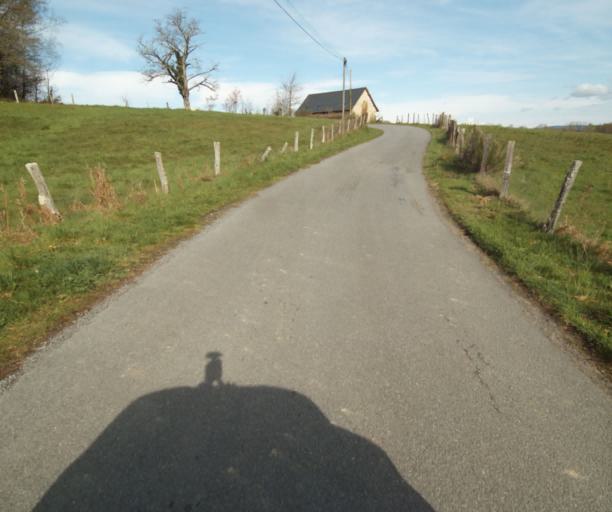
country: FR
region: Limousin
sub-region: Departement de la Correze
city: Correze
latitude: 45.3395
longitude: 1.8333
